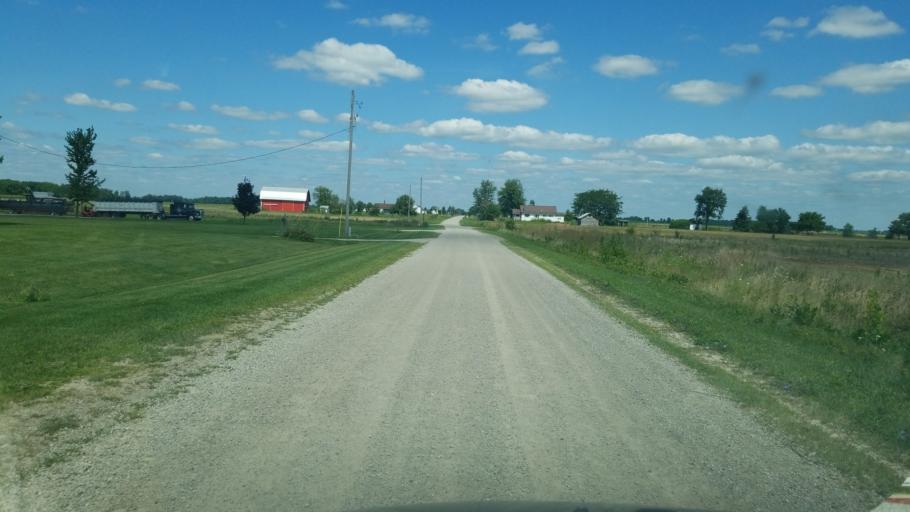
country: US
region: Ohio
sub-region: Fulton County
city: Delta
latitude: 41.7267
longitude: -84.0184
